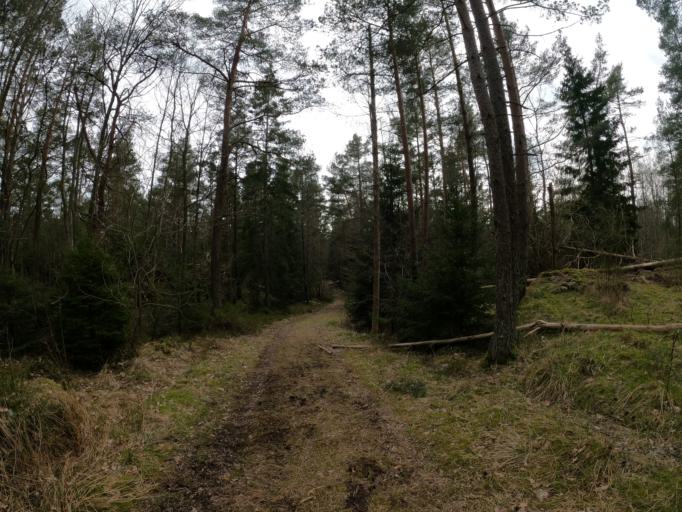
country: SE
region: Vaestra Goetaland
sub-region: Molndal
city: Kallered
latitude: 57.6278
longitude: 12.0798
